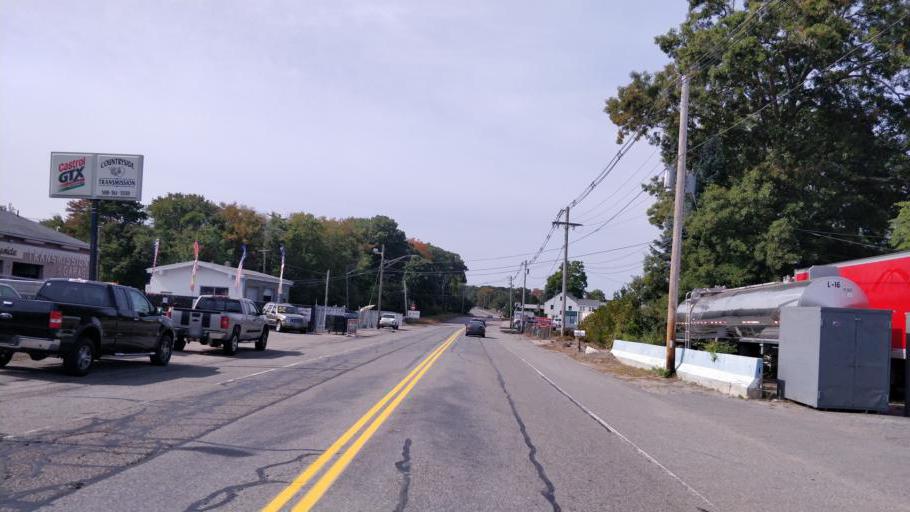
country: US
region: Massachusetts
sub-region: Bristol County
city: North Seekonk
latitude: 41.9030
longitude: -71.3397
